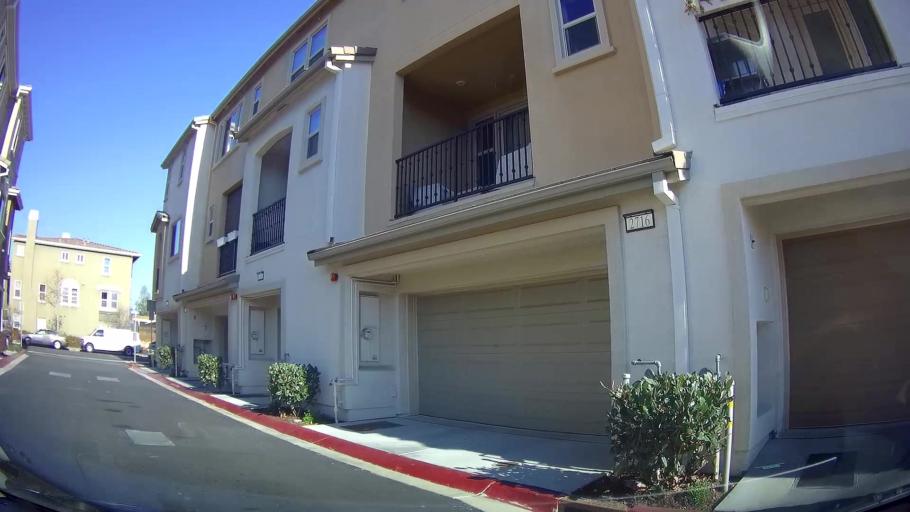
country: US
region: California
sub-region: Santa Clara County
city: Seven Trees
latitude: 37.2909
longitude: -121.8565
